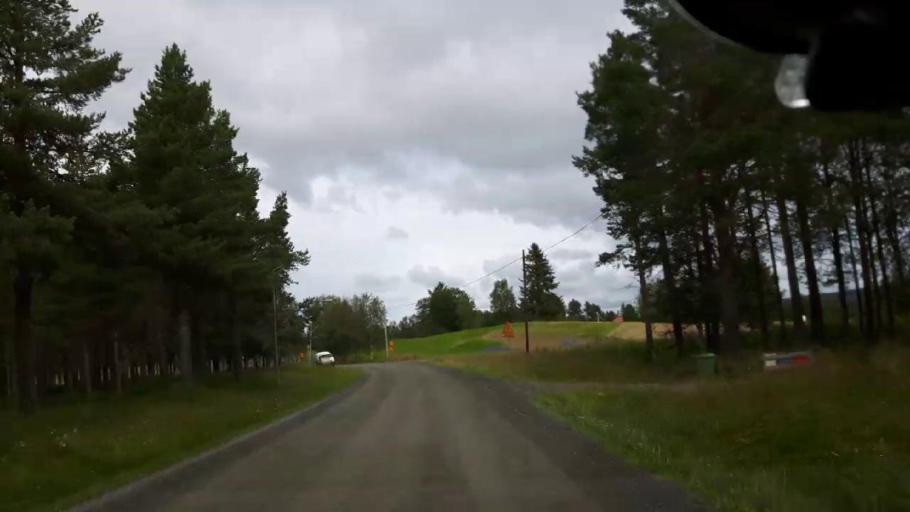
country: SE
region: Jaemtland
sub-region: Krokoms Kommun
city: Valla
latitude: 63.4076
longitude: 14.0930
